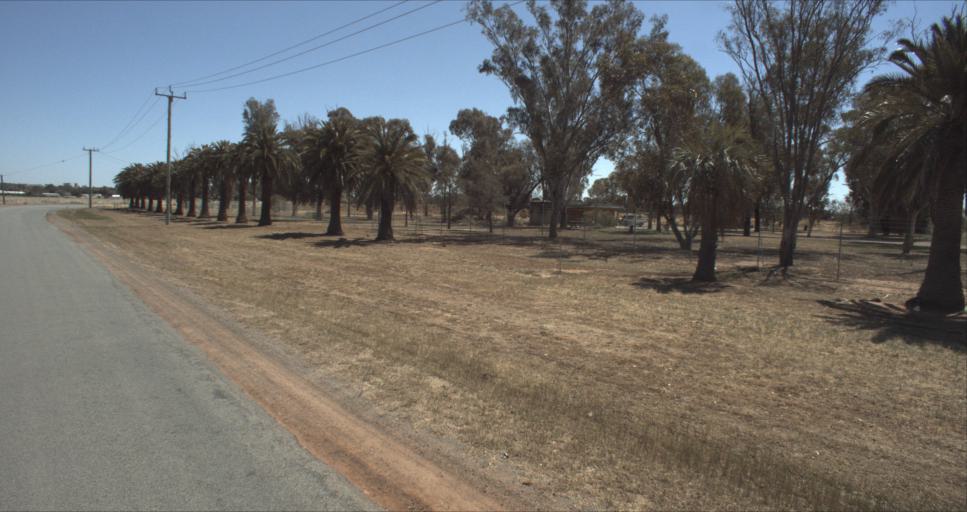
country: AU
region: New South Wales
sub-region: Leeton
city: Leeton
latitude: -34.5444
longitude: 146.4274
